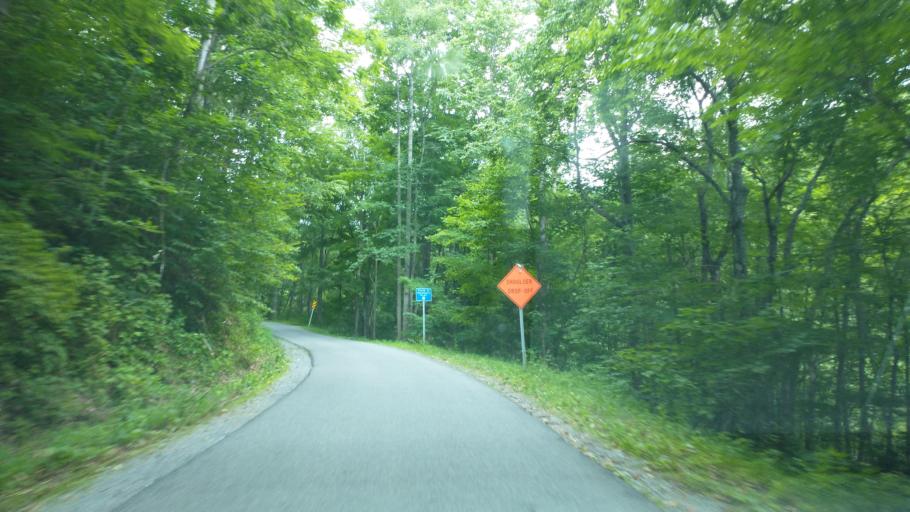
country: US
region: West Virginia
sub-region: Mercer County
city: Athens
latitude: 37.4636
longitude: -81.0644
